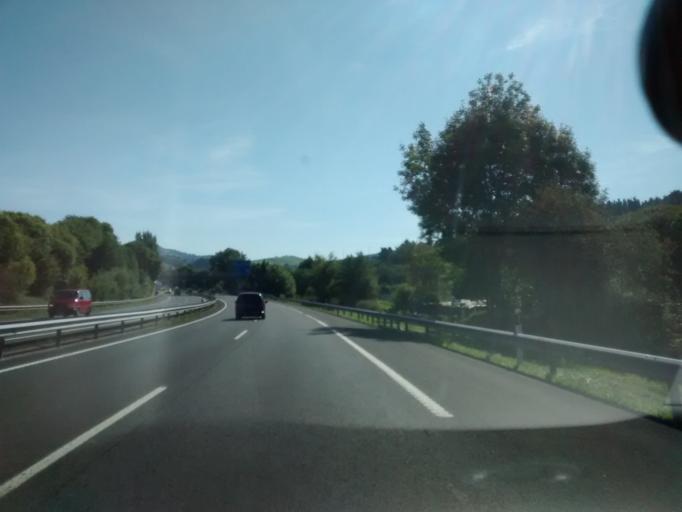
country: ES
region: Basque Country
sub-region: Provincia de Guipuzcoa
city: Zarautz
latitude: 43.2783
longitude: -2.1697
